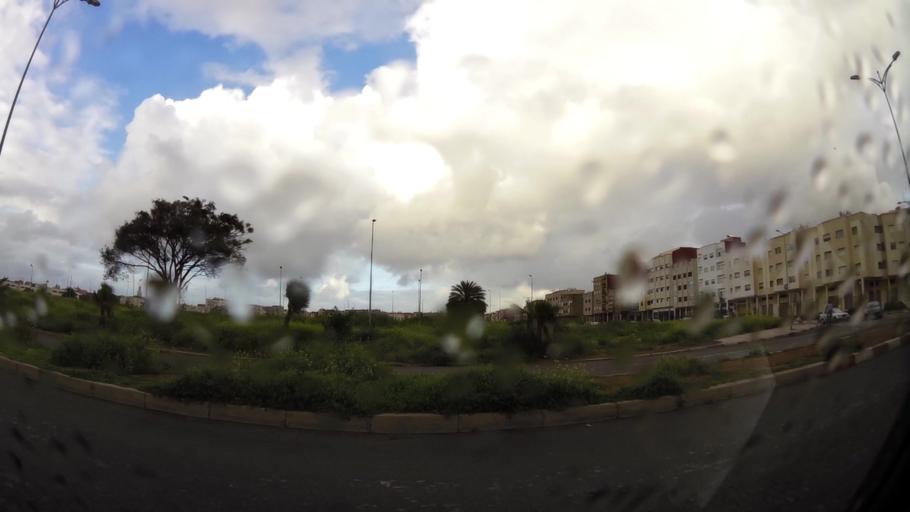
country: MA
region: Grand Casablanca
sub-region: Mohammedia
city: Mohammedia
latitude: 33.6818
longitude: -7.3837
